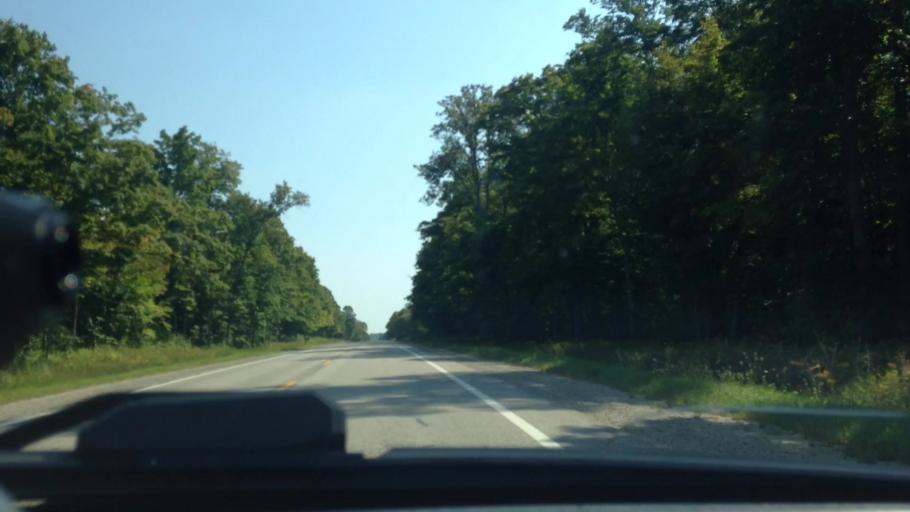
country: US
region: Michigan
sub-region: Luce County
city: Newberry
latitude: 46.3230
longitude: -85.6695
